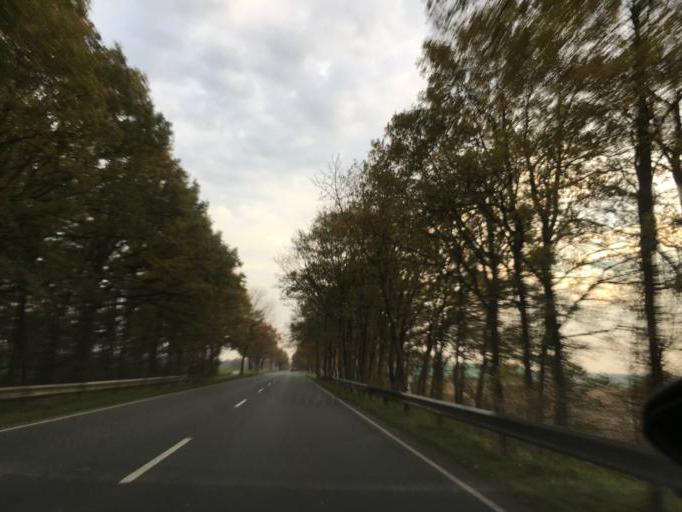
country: DE
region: Lower Saxony
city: Bergen
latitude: 52.7850
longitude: 9.9743
